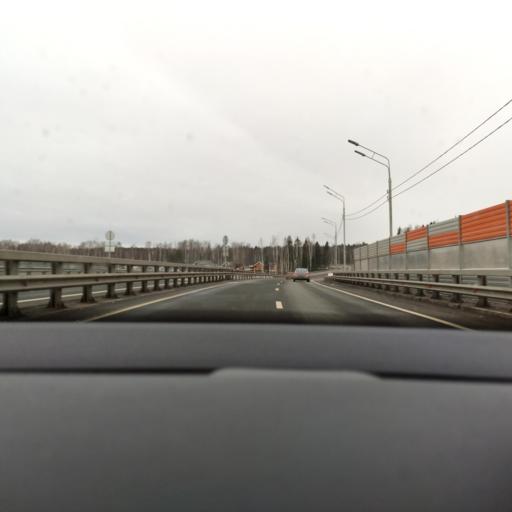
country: RU
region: Moskovskaya
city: Bol'shiye Vyazemy
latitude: 55.6464
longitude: 36.9889
